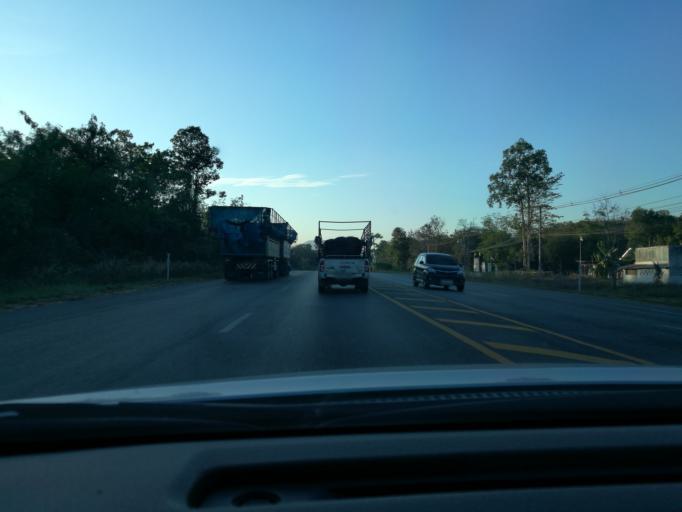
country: TH
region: Phitsanulok
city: Wang Thong
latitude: 16.8465
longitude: 100.5246
